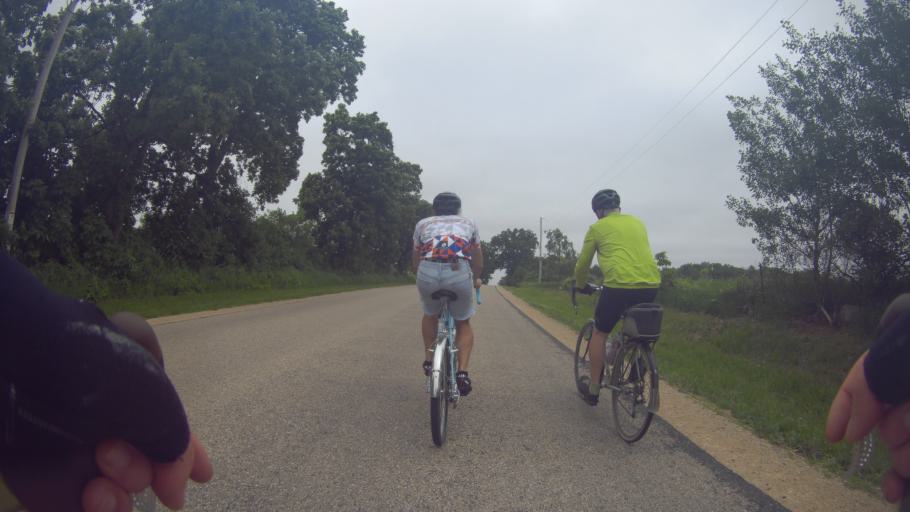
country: US
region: Wisconsin
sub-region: Green County
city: Brooklyn
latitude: 42.8636
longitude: -89.4135
